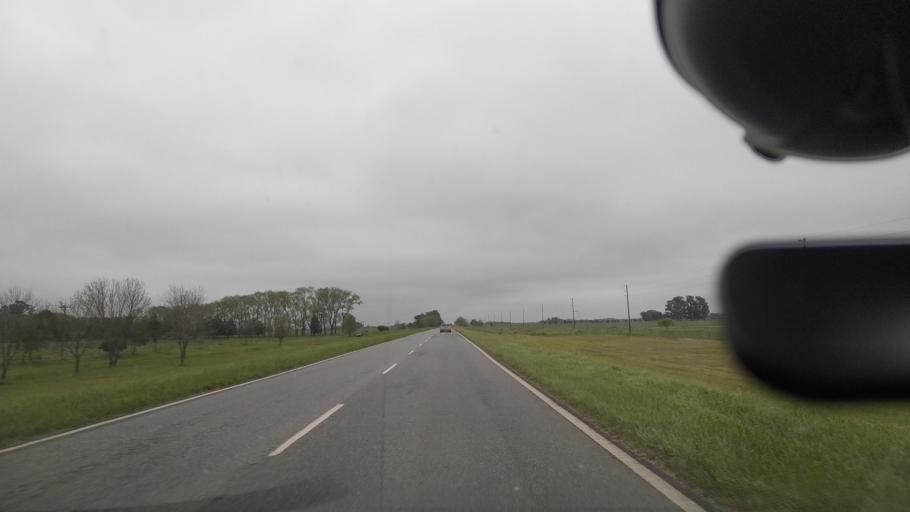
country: AR
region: Buenos Aires
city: Veronica
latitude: -35.3012
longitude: -57.5105
